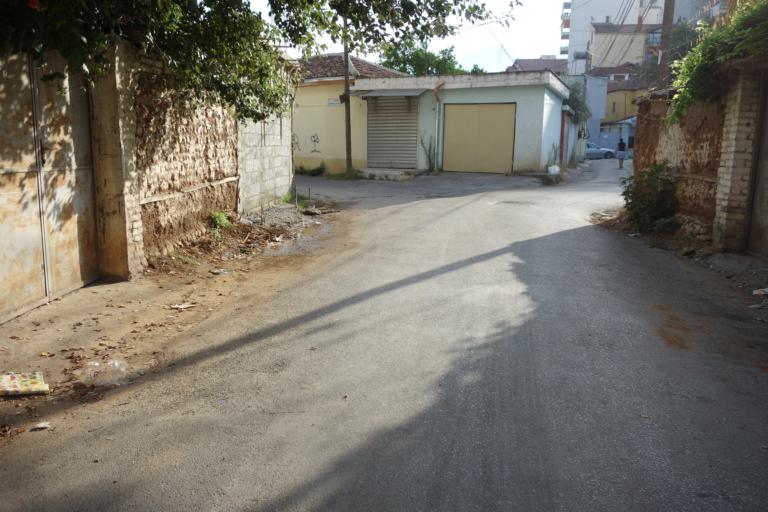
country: AL
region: Tirane
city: Tirana
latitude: 41.3336
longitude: 19.8202
